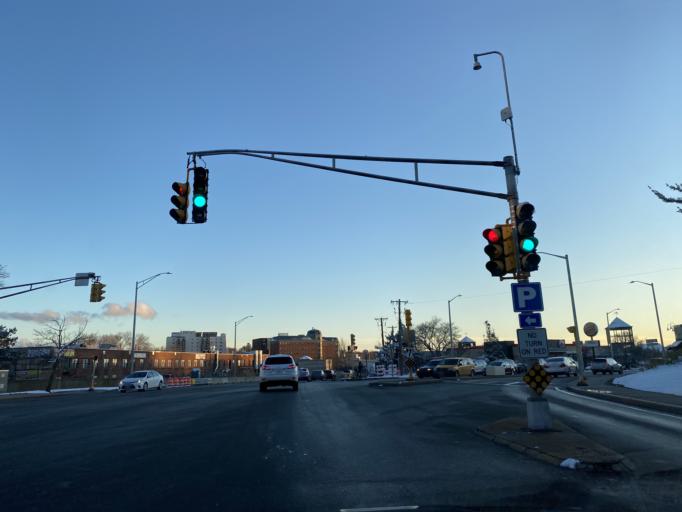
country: US
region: Massachusetts
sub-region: Norfolk County
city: Quincy
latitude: 42.2488
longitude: -71.0041
